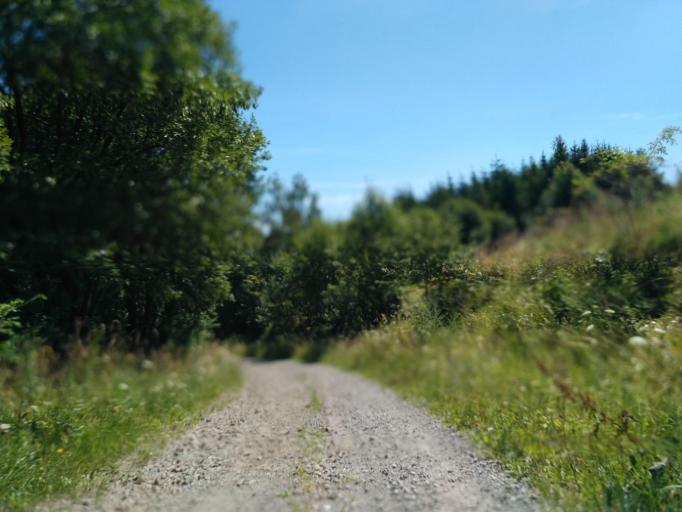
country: PL
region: Subcarpathian Voivodeship
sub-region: Powiat sanocki
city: Bukowsko
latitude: 49.5033
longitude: 22.0630
